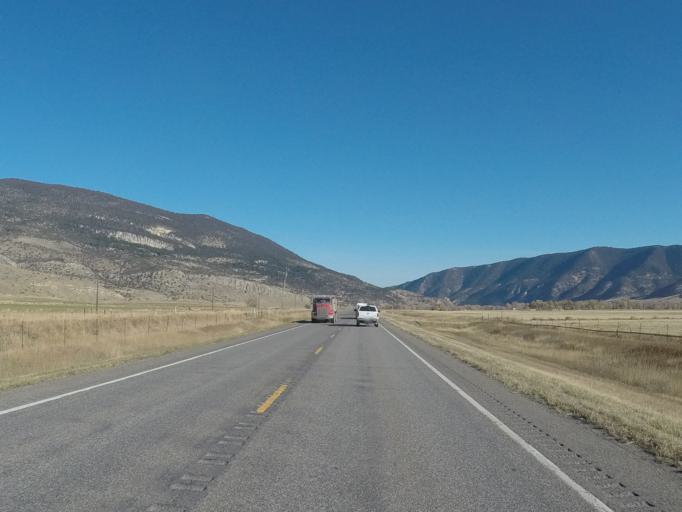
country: US
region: Montana
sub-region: Park County
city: Livingston
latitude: 45.5539
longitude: -110.5959
